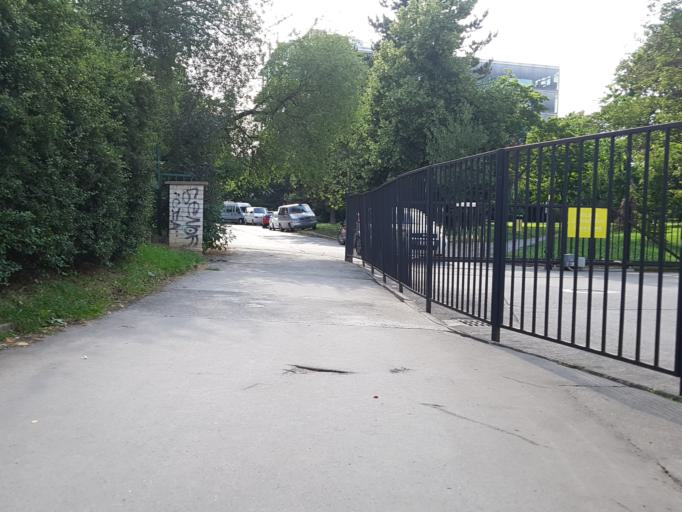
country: CZ
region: Praha
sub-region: Praha 8
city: Liben
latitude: 50.0717
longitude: 14.4914
